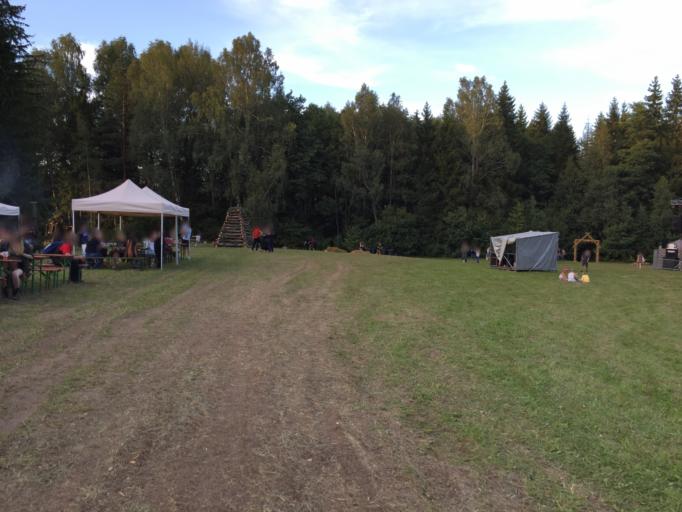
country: LT
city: Zarasai
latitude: 55.7911
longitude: 25.9603
